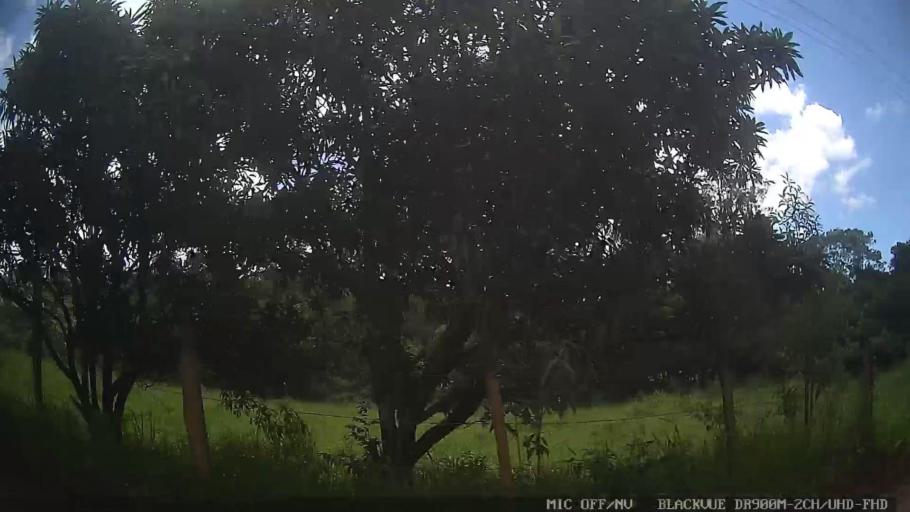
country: BR
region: Sao Paulo
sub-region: Piracaia
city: Piracaia
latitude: -23.0208
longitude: -46.4583
